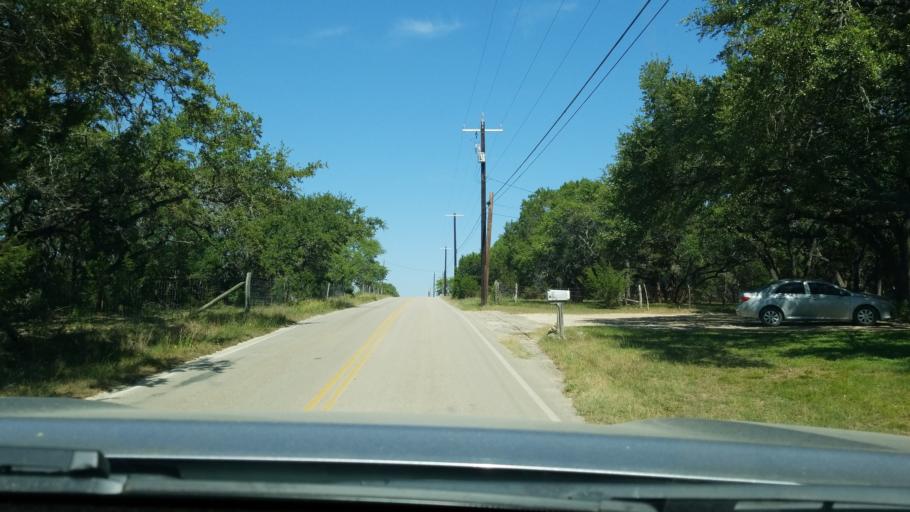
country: US
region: Texas
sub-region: Comal County
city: Bulverde
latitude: 29.7591
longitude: -98.5017
